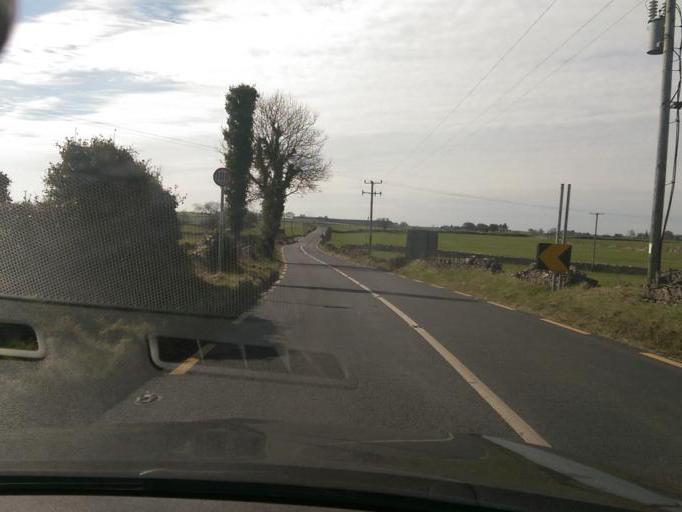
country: IE
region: Connaught
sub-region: County Galway
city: Athenry
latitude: 53.4877
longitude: -8.5824
